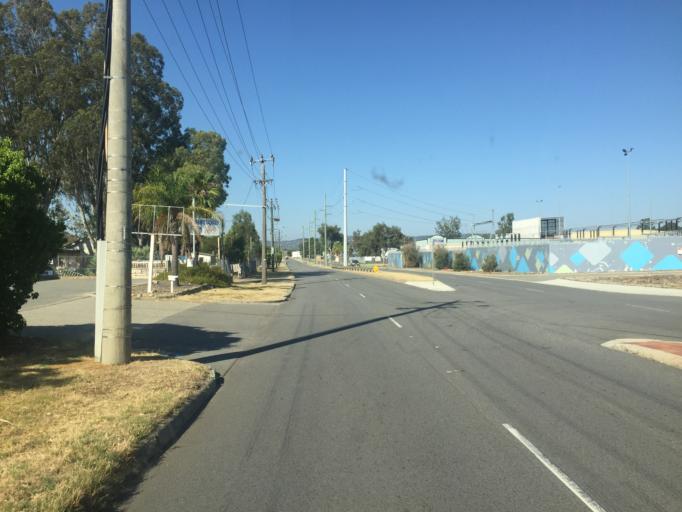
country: AU
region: Western Australia
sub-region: Gosnells
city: Maddington
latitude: -32.0449
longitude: 115.9775
